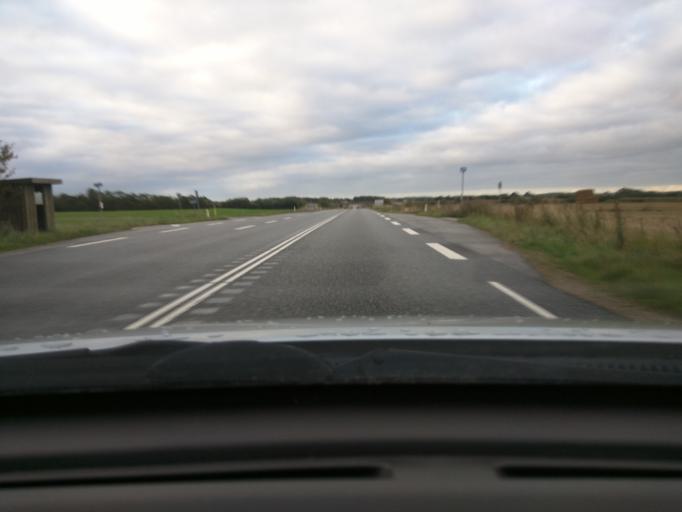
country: DK
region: Central Jutland
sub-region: Silkeborg Kommune
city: Kjellerup
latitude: 56.3047
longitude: 9.3246
